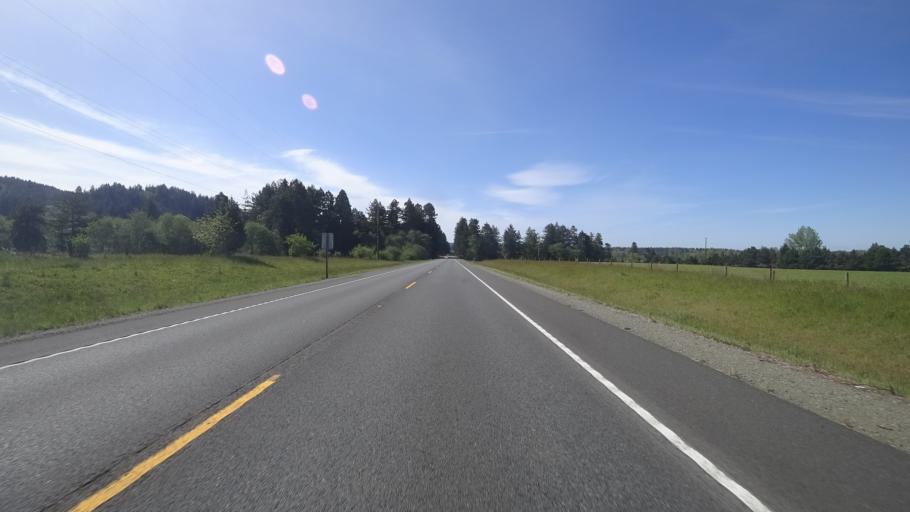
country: US
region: California
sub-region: Del Norte County
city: Bertsch-Oceanview
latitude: 41.8904
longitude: -124.1367
